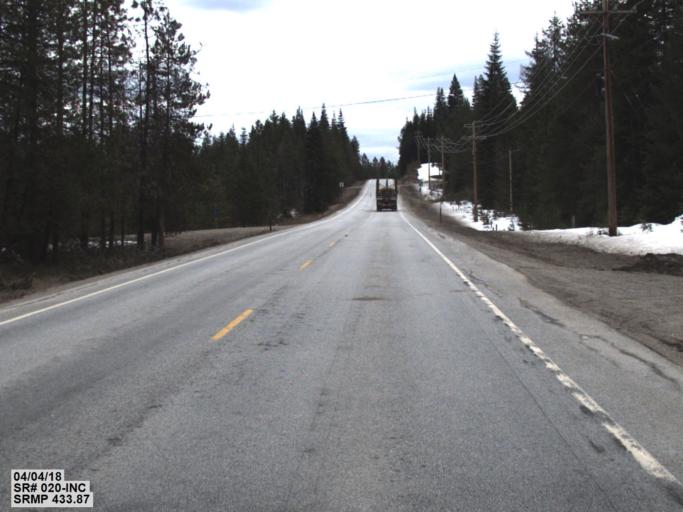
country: US
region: Washington
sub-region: Pend Oreille County
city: Newport
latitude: 48.2167
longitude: -117.0807
